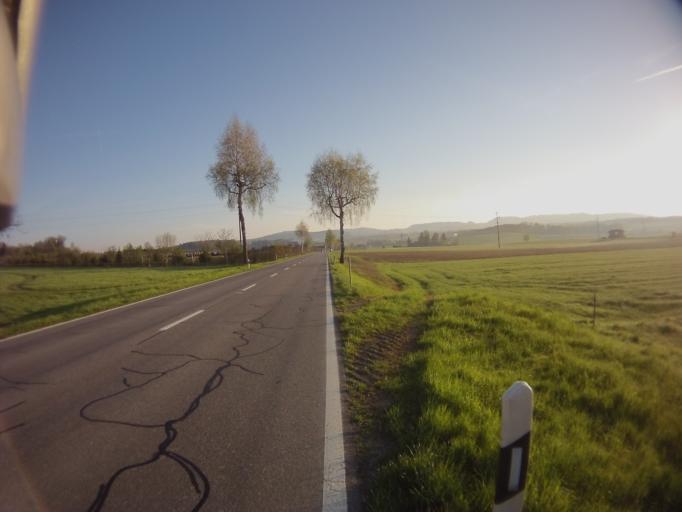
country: CH
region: Zug
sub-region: Zug
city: Cham
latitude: 47.2023
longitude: 8.4544
